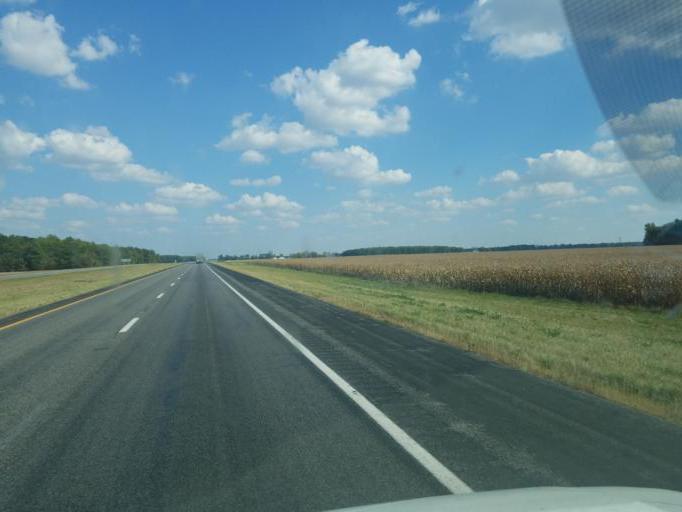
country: US
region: Ohio
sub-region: Hardin County
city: Ada
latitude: 40.8260
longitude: -83.7802
